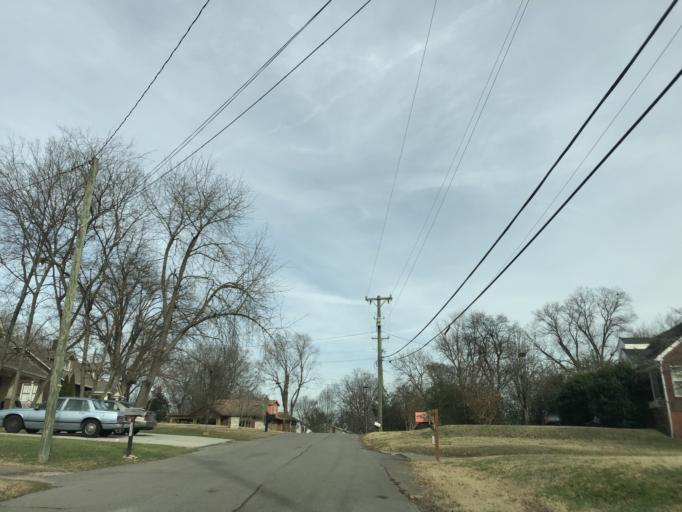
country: US
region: Tennessee
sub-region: Davidson County
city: Nashville
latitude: 36.2102
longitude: -86.7224
